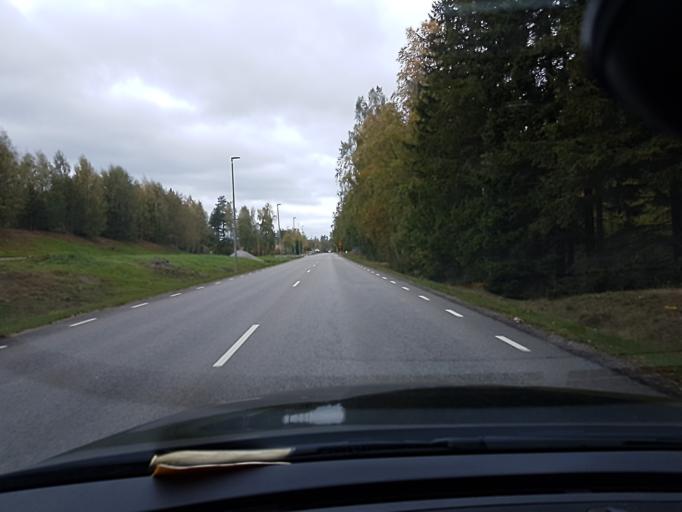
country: SE
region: Kronoberg
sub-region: Vaxjo Kommun
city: Vaexjoe
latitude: 56.9117
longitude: 14.8180
